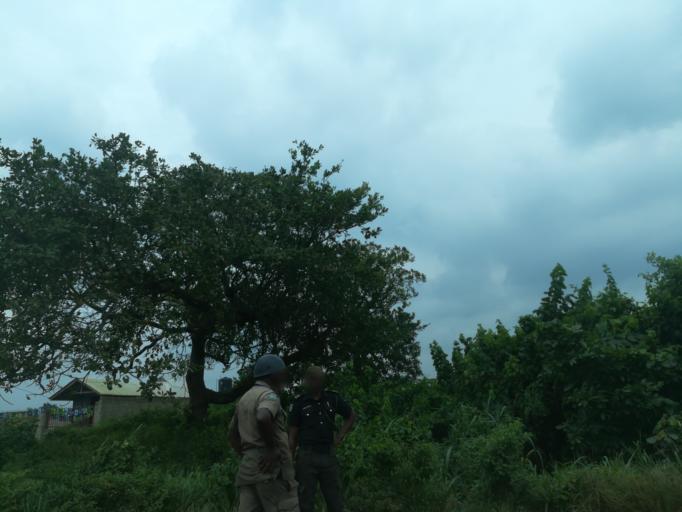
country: NG
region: Lagos
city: Ejirin
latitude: 6.6456
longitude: 3.7292
